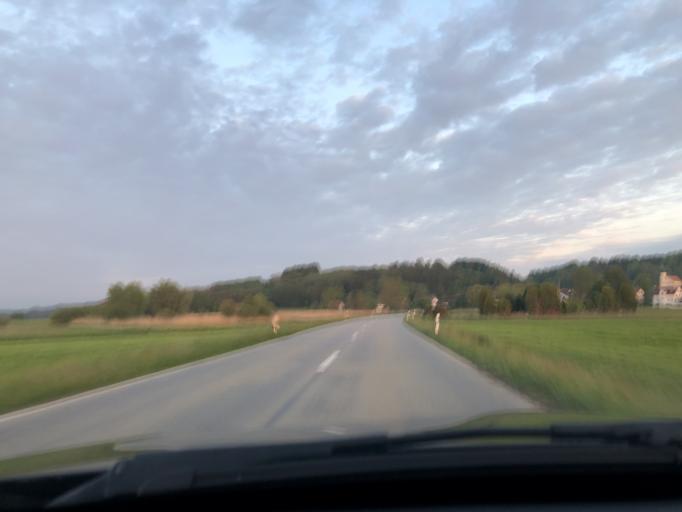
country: DE
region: Bavaria
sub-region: Upper Bavaria
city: Wolfersdorf
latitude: 48.4446
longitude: 11.7201
